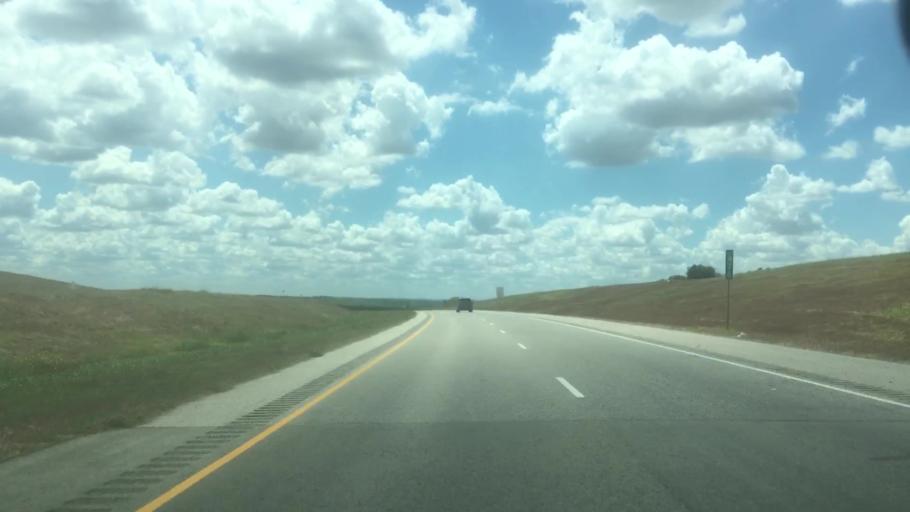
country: US
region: Texas
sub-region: Caldwell County
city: Lockhart
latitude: 29.8500
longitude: -97.7244
